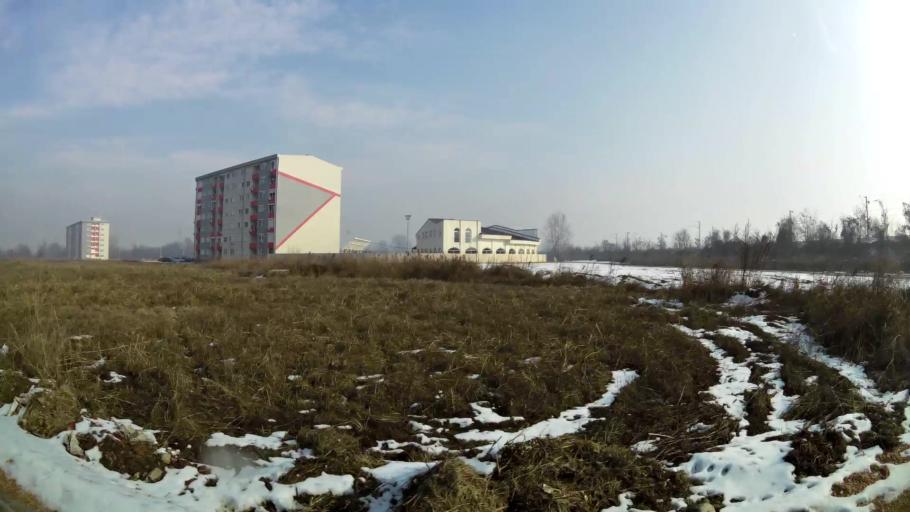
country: MK
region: Kisela Voda
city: Kisela Voda
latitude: 41.9915
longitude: 21.5171
